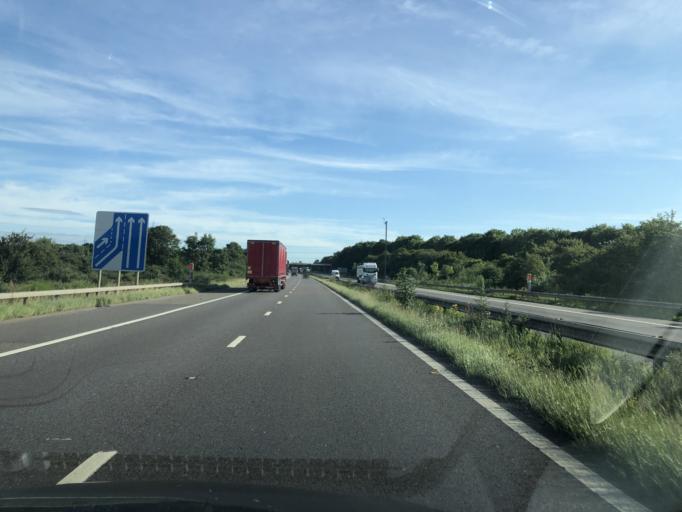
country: GB
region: England
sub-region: Rotherham
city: Bramley
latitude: 53.3970
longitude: -1.2688
